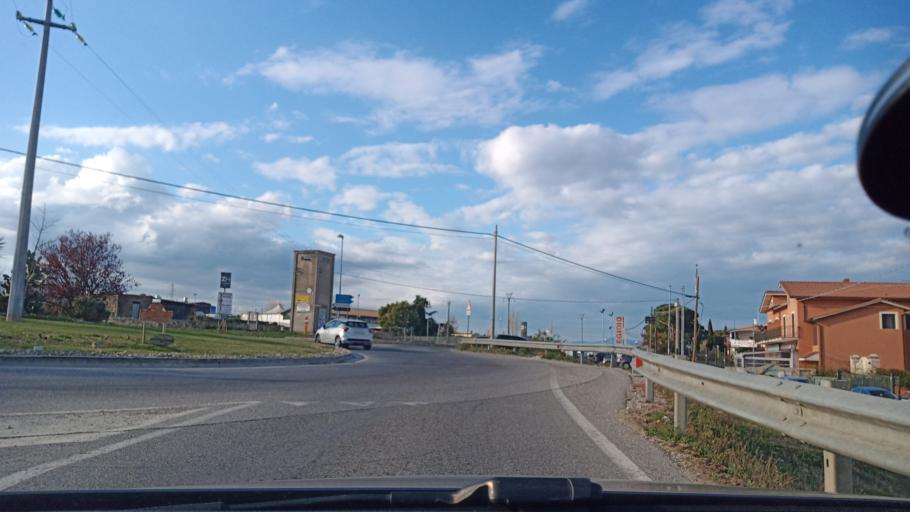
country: IT
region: Latium
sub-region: Citta metropolitana di Roma Capitale
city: Fiano Romano
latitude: 42.1513
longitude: 12.6159
